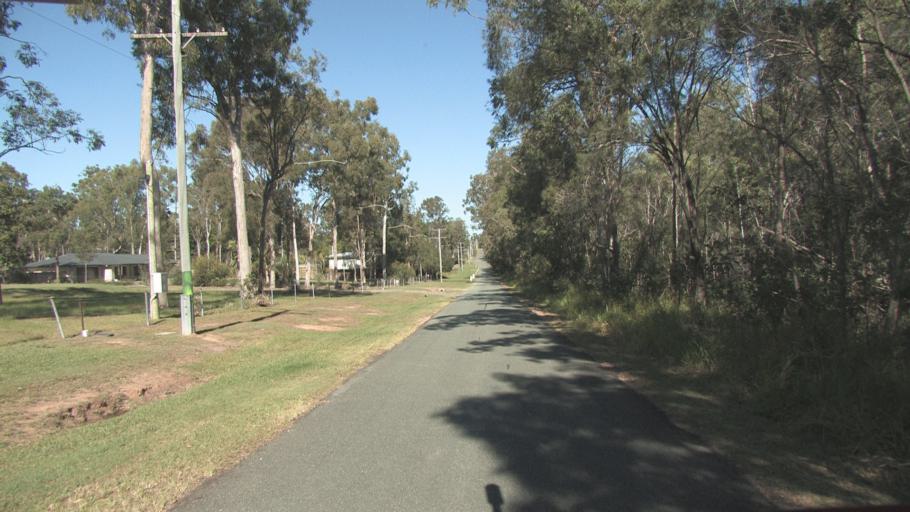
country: AU
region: Queensland
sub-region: Logan
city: Park Ridge South
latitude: -27.6948
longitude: 153.0047
